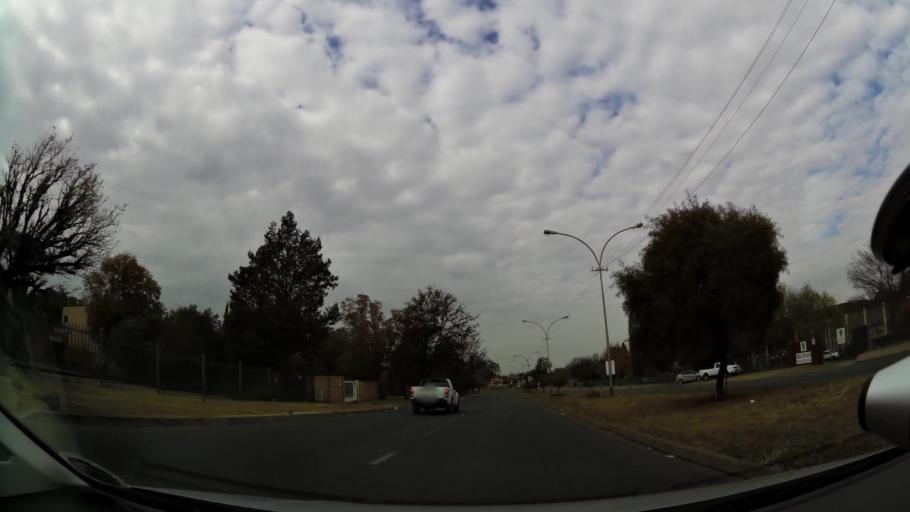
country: ZA
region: Orange Free State
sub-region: Mangaung Metropolitan Municipality
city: Bloemfontein
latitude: -29.0837
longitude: 26.2236
